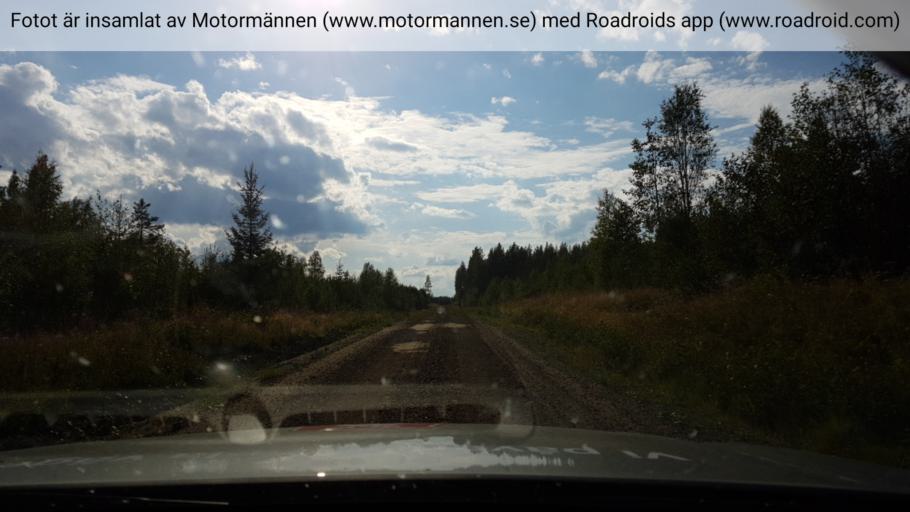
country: SE
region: Jaemtland
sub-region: Stroemsunds Kommun
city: Stroemsund
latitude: 63.7207
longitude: 16.0626
